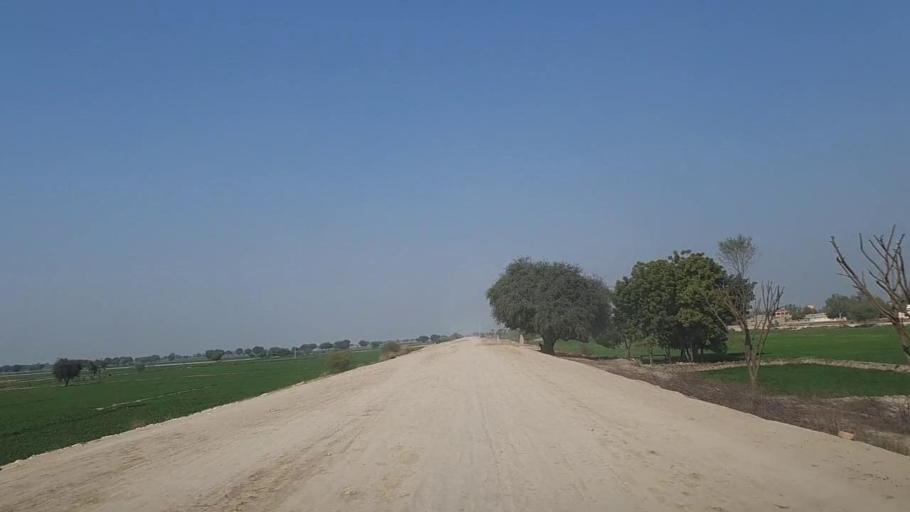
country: PK
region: Sindh
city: Moro
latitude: 26.7361
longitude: 67.9183
